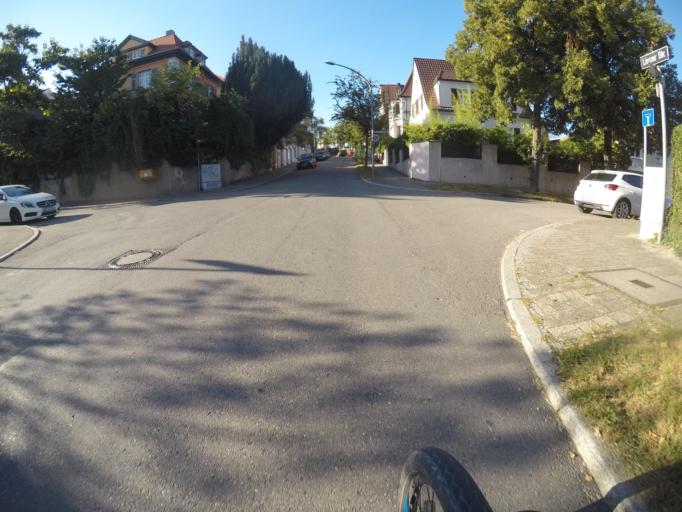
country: DE
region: Baden-Wuerttemberg
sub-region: Regierungsbezirk Stuttgart
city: Stuttgart Feuerbach
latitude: 48.8139
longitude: 9.1541
